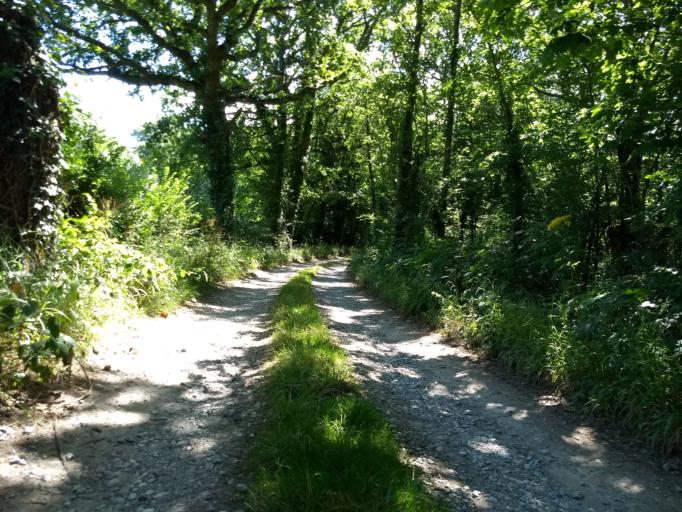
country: GB
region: England
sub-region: Isle of Wight
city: Newport
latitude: 50.7196
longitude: -1.2689
